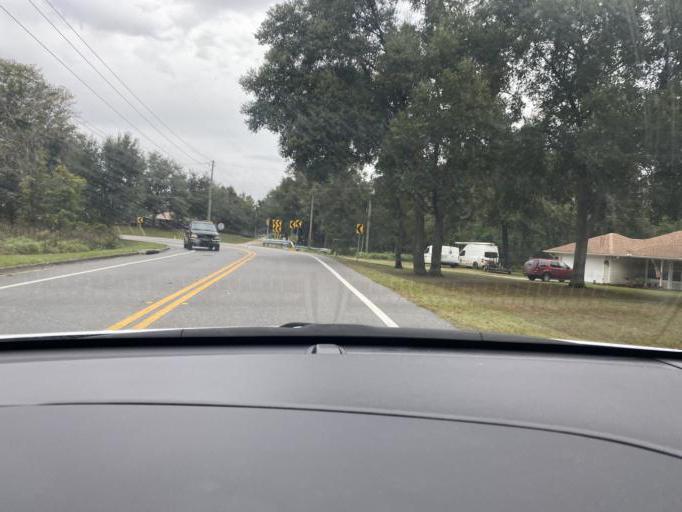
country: US
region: Florida
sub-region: Lake County
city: Groveland
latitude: 28.5763
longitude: -81.8597
